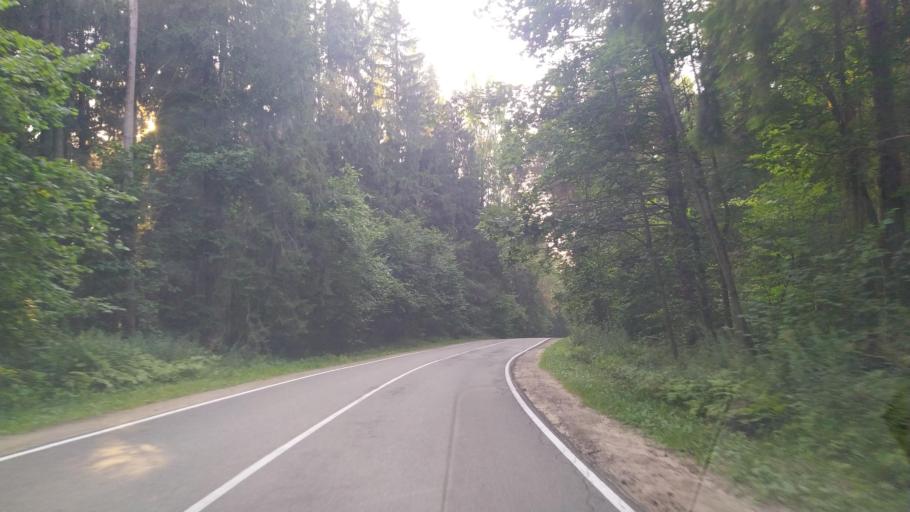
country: RU
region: Pskov
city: Pushkinskiye Gory
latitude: 57.0348
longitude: 28.9165
